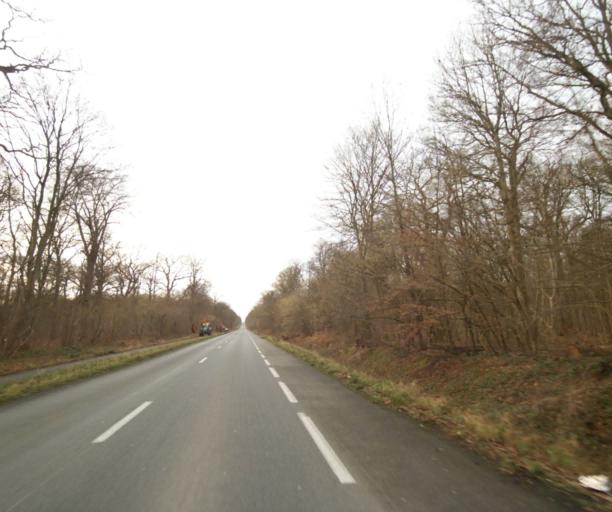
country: BE
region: Wallonia
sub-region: Province du Hainaut
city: Peruwelz
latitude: 50.4900
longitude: 3.6045
